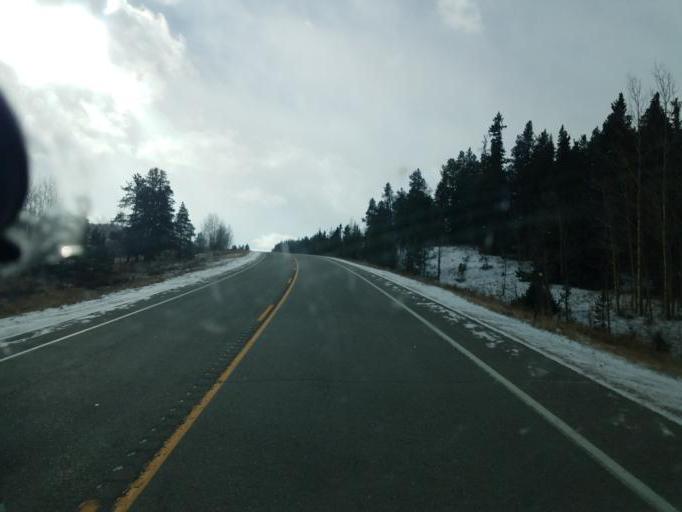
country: US
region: Colorado
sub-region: Summit County
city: Breckenridge
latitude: 39.4192
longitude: -105.7646
